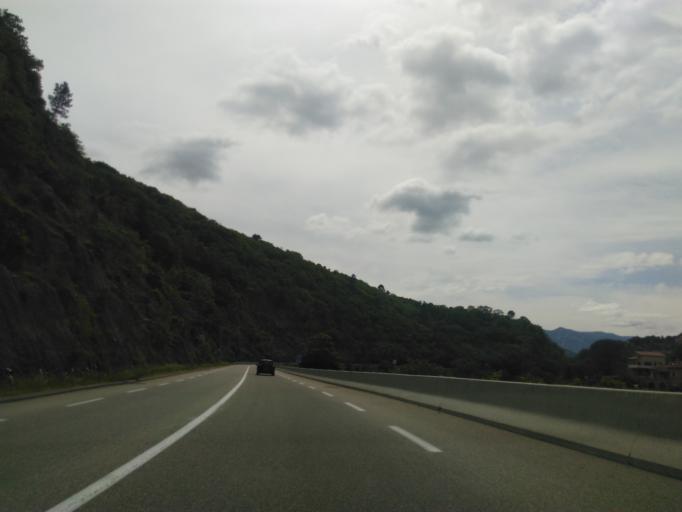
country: FR
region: Rhone-Alpes
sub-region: Departement de l'Ardeche
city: Labegude
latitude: 44.6482
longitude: 4.3628
